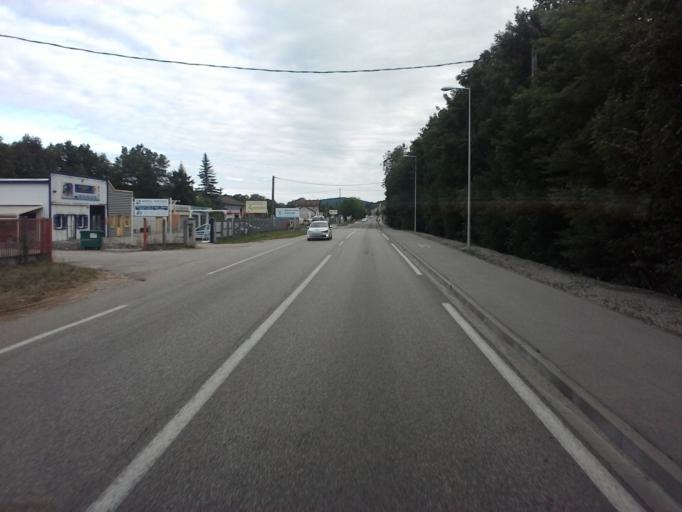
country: FR
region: Rhone-Alpes
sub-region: Departement de l'Ain
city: Ambronay
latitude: 46.0414
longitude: 5.3368
